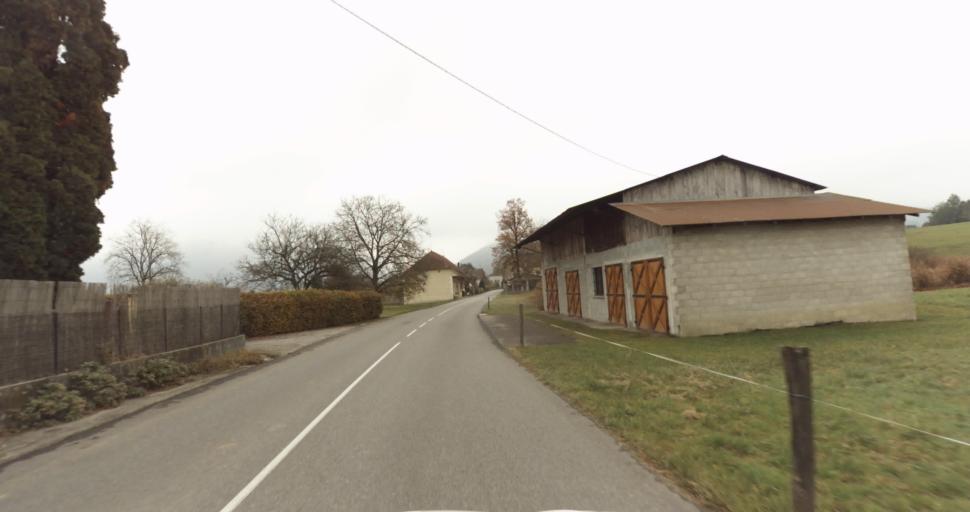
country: FR
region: Rhone-Alpes
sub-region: Departement de la Haute-Savoie
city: Cusy
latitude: 45.7749
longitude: 6.0214
